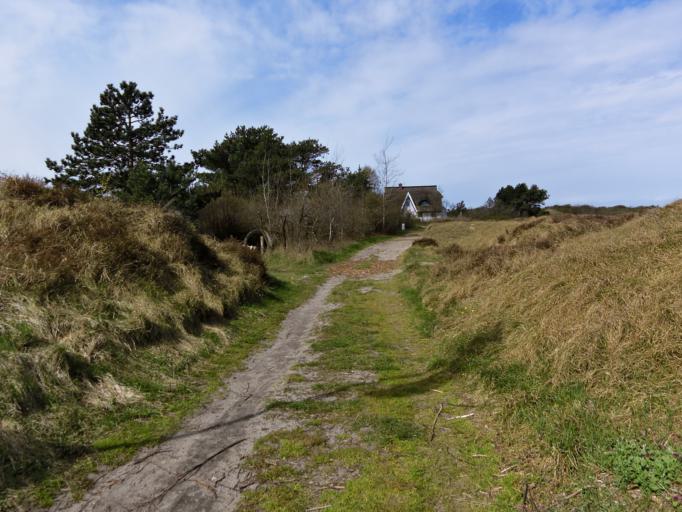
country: DE
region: Mecklenburg-Vorpommern
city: Hiddensee
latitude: 54.5480
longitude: 13.0971
